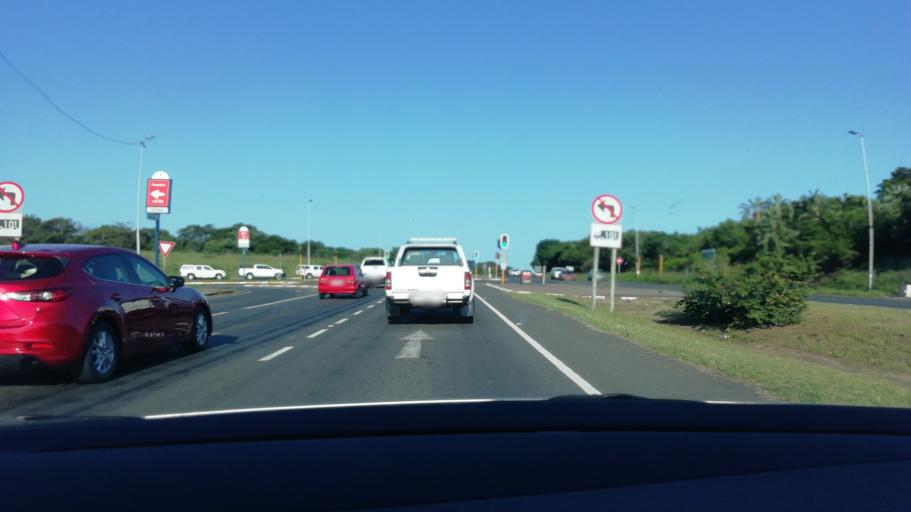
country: ZA
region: KwaZulu-Natal
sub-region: uThungulu District Municipality
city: Richards Bay
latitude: -28.7682
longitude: 32.0481
